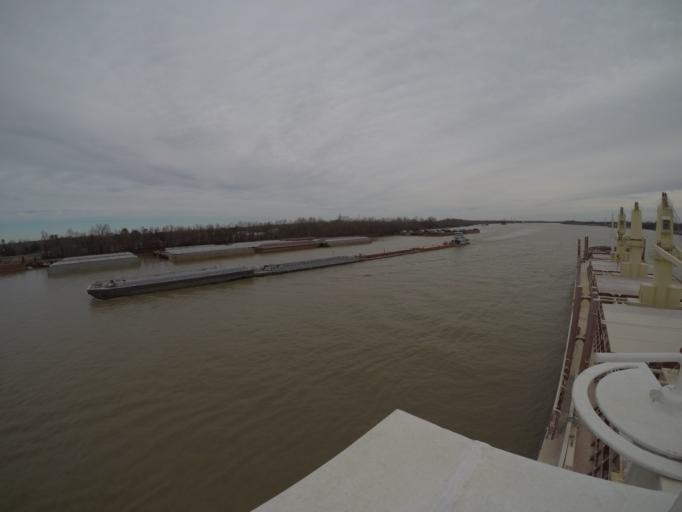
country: US
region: Louisiana
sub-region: Saint John the Baptist Parish
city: Reserve
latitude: 30.0467
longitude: -90.5342
